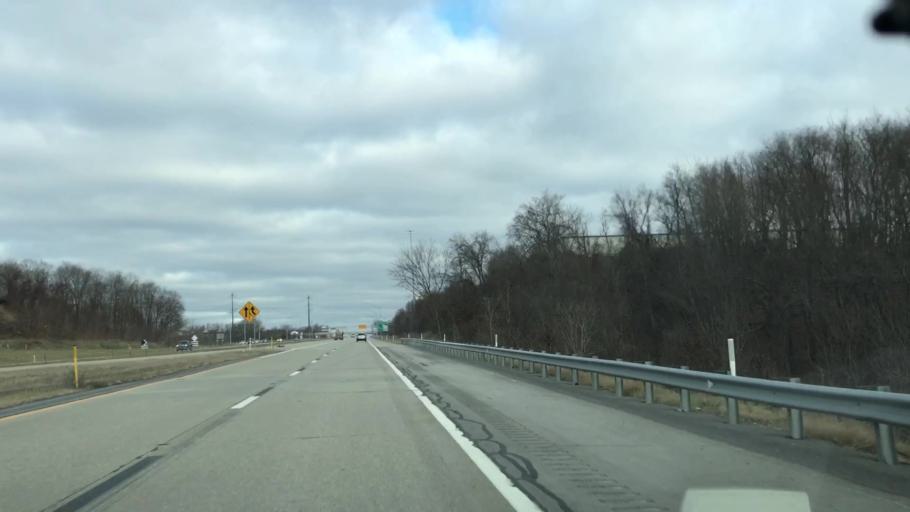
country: US
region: Pennsylvania
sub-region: Allegheny County
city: Carnot-Moon
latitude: 40.5243
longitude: -80.2722
